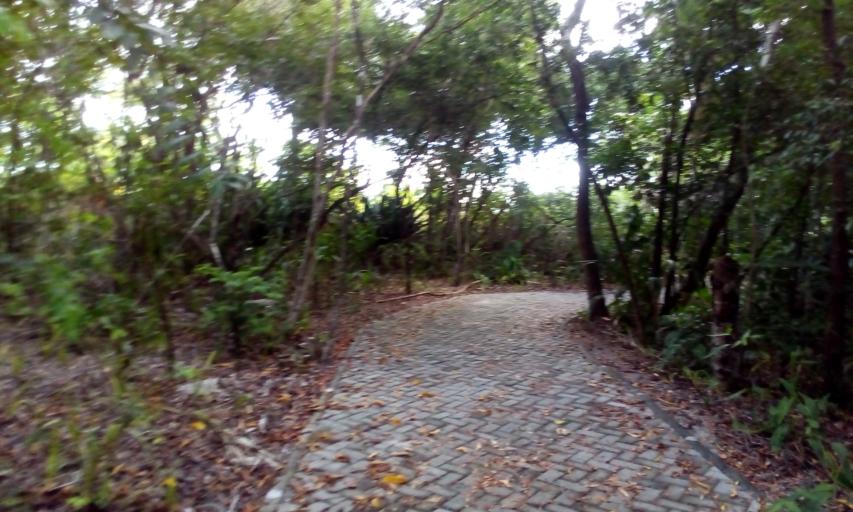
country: BR
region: Bahia
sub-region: Mata De Sao Joao
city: Mata de Sao Joao
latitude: -12.5656
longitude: -38.0011
